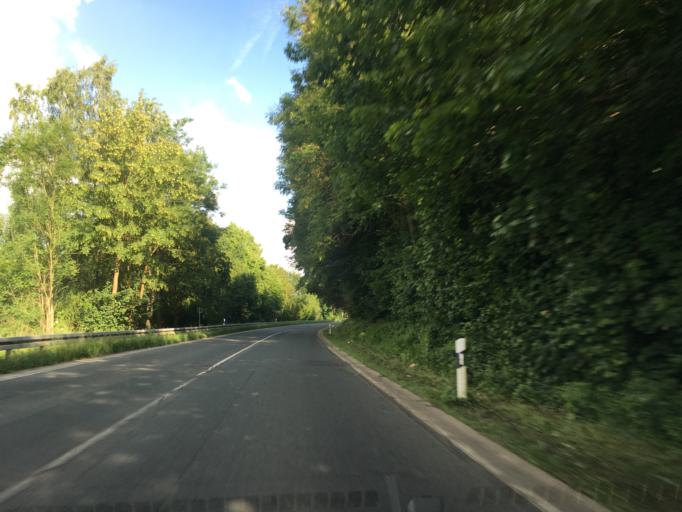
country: DE
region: North Rhine-Westphalia
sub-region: Regierungsbezirk Munster
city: Altenberge
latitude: 52.0555
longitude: 7.4612
